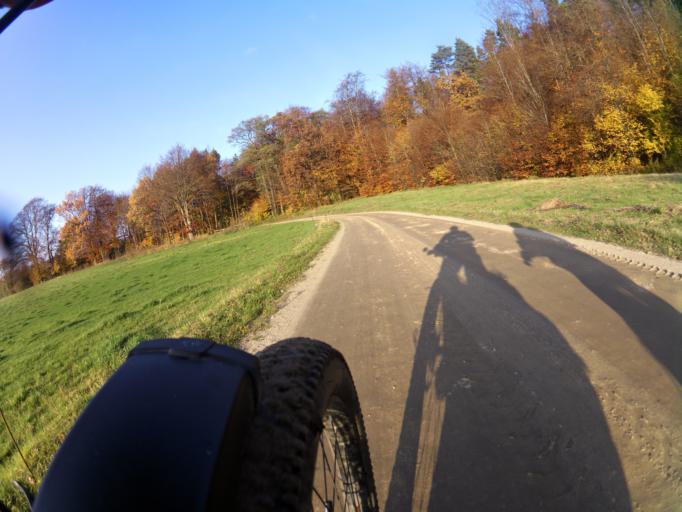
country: PL
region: Pomeranian Voivodeship
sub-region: Powiat pucki
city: Krokowa
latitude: 54.7491
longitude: 18.1961
